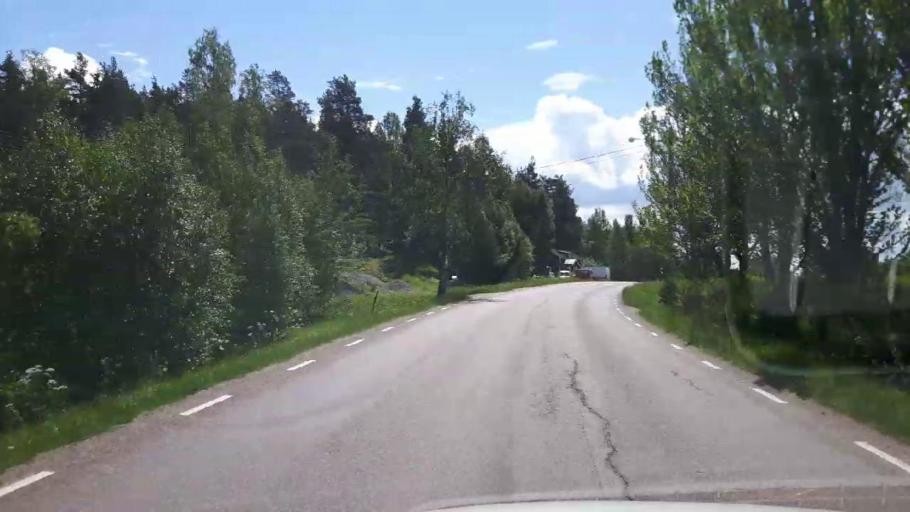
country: SE
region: Dalarna
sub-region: Faluns Kommun
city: Falun
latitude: 60.6027
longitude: 15.7682
